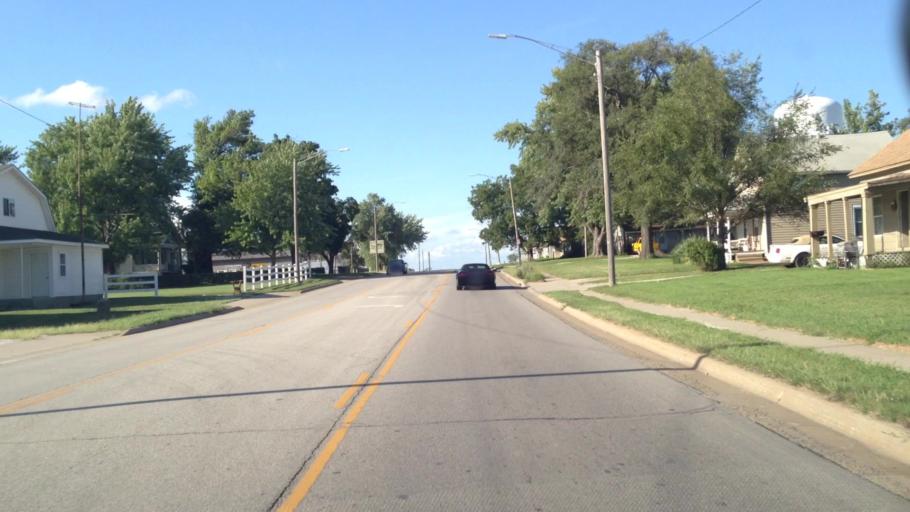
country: US
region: Kansas
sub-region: Franklin County
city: Ottawa
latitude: 38.6308
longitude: -95.2677
